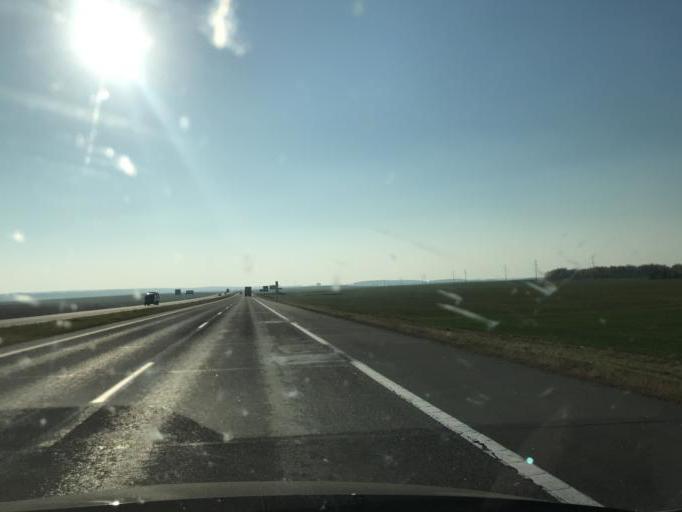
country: BY
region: Minsk
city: Snow
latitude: 53.3186
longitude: 26.4035
